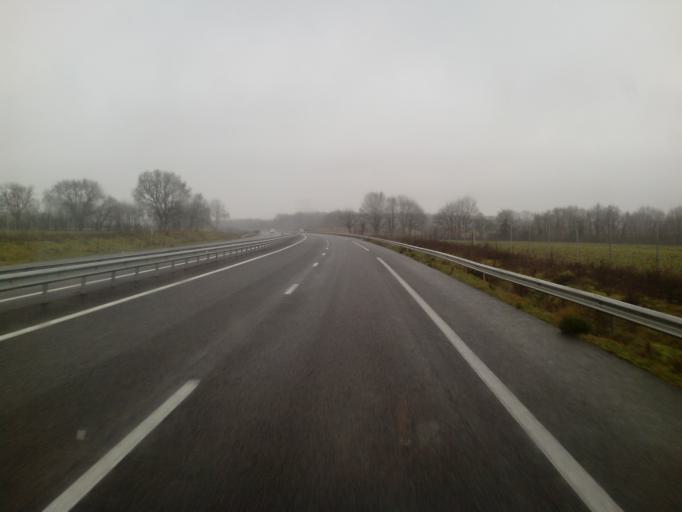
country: FR
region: Poitou-Charentes
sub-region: Departement de la Vienne
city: Terce
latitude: 46.4788
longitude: 0.5384
